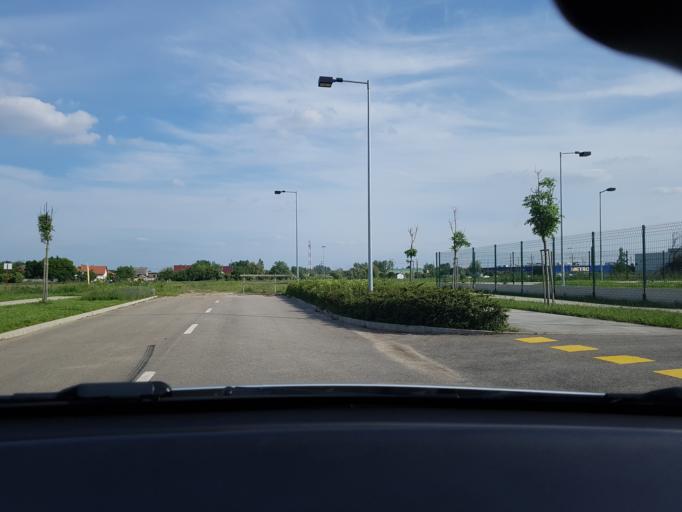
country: HU
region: Csongrad
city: Szeged
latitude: 46.2774
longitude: 20.1059
